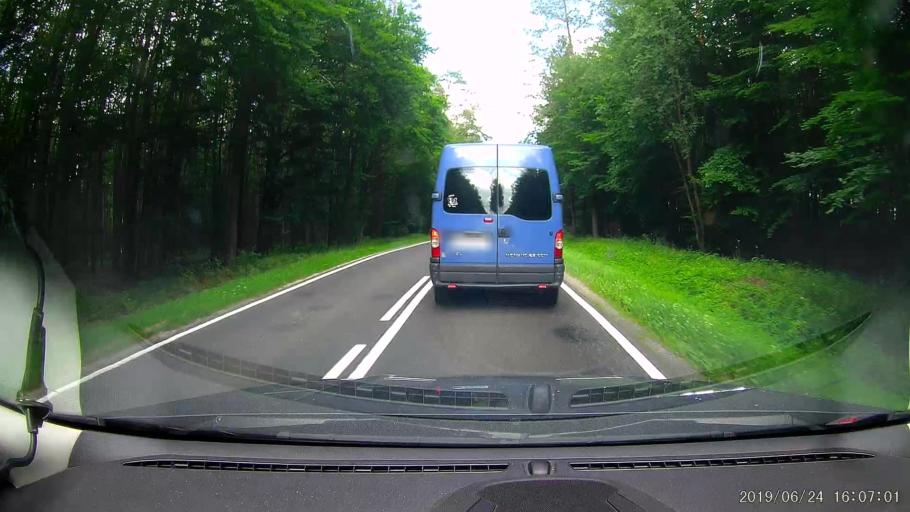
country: PL
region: Subcarpathian Voivodeship
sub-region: Powiat lubaczowski
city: Narol
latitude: 50.3436
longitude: 23.3141
